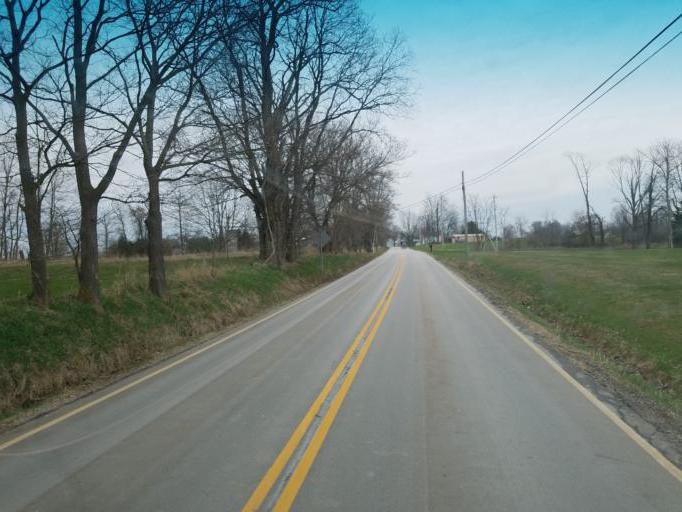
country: US
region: Ohio
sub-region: Crawford County
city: Galion
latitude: 40.7098
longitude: -82.7207
